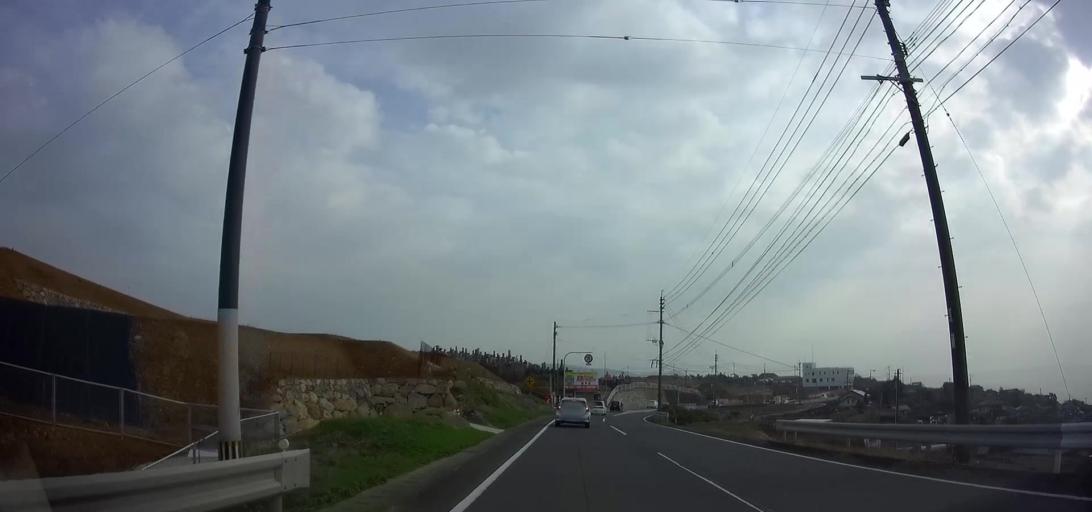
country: JP
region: Nagasaki
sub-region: Isahaya-shi
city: Isahaya
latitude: 32.7915
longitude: 130.0627
